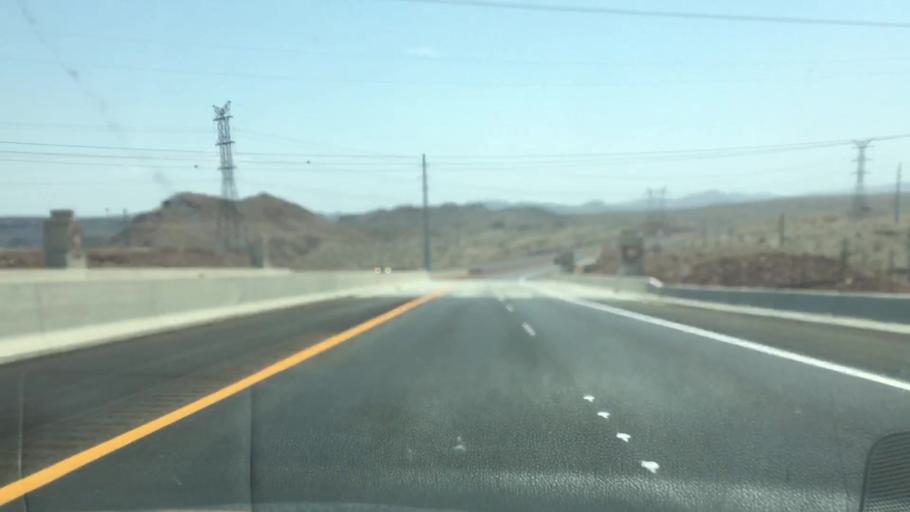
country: US
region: Nevada
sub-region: Clark County
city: Boulder City
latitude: 35.9829
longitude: -114.7940
